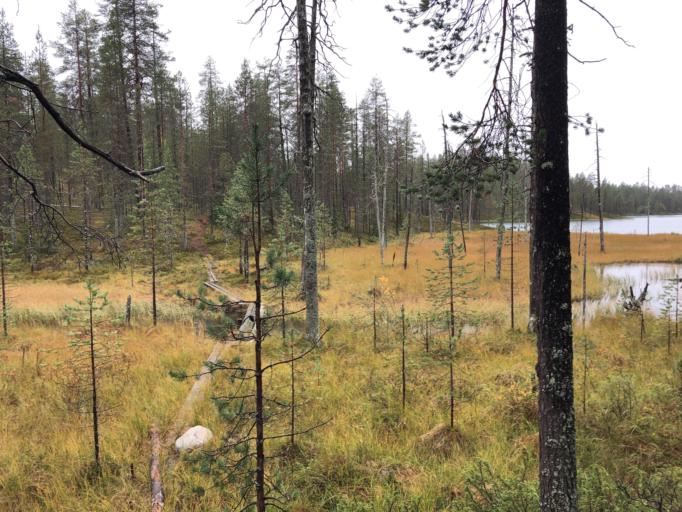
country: FI
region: Lapland
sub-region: Itae-Lappi
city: Posio
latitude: 66.0694
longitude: 27.7642
